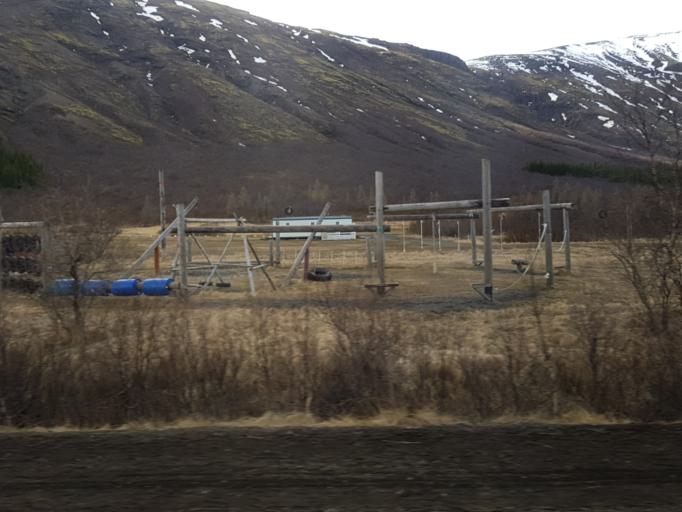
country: IS
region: South
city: Selfoss
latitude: 64.2219
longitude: -20.7286
